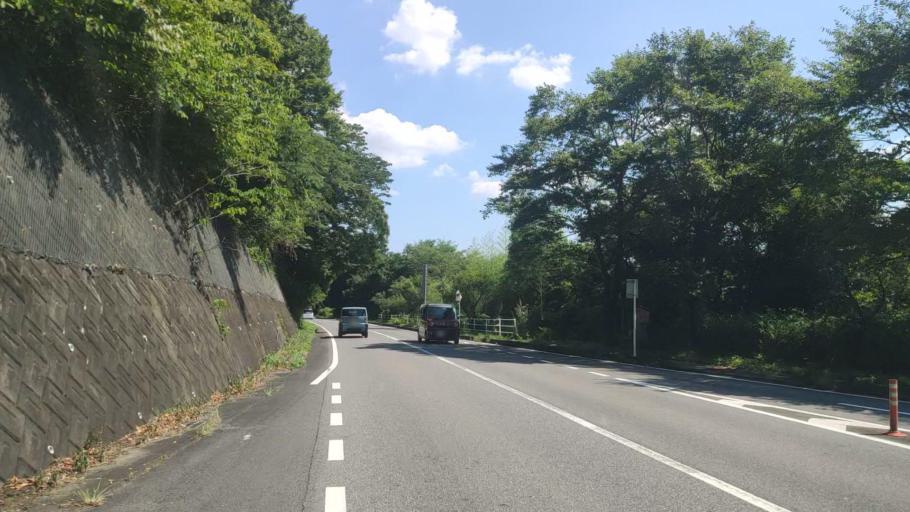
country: JP
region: Gifu
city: Godo
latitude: 35.5029
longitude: 136.6662
